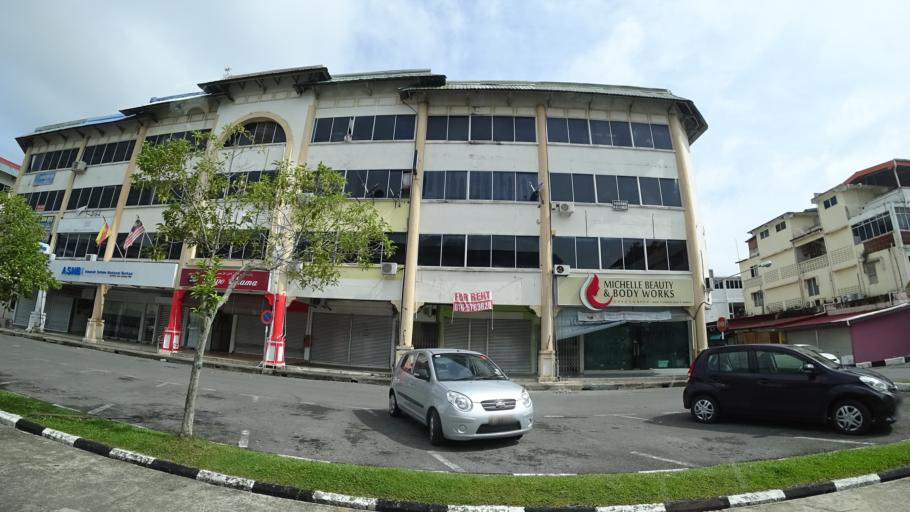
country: MY
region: Sarawak
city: Miri
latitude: 4.3987
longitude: 113.9870
